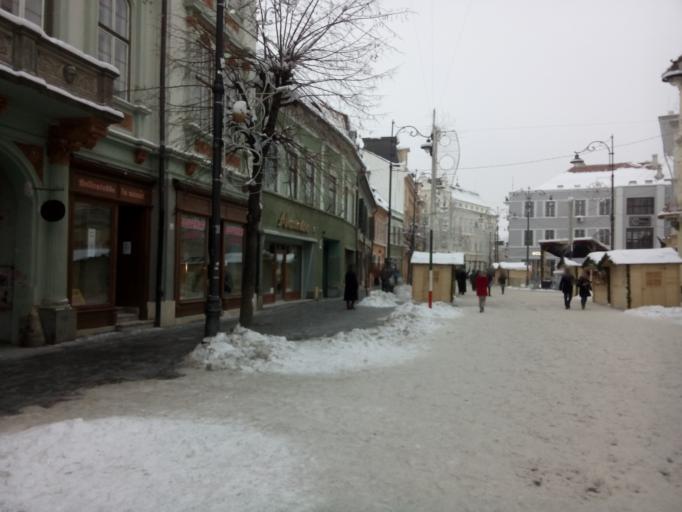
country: RO
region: Sibiu
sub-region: Municipiul Sibiu
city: Sibiu
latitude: 45.7944
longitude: 24.1503
